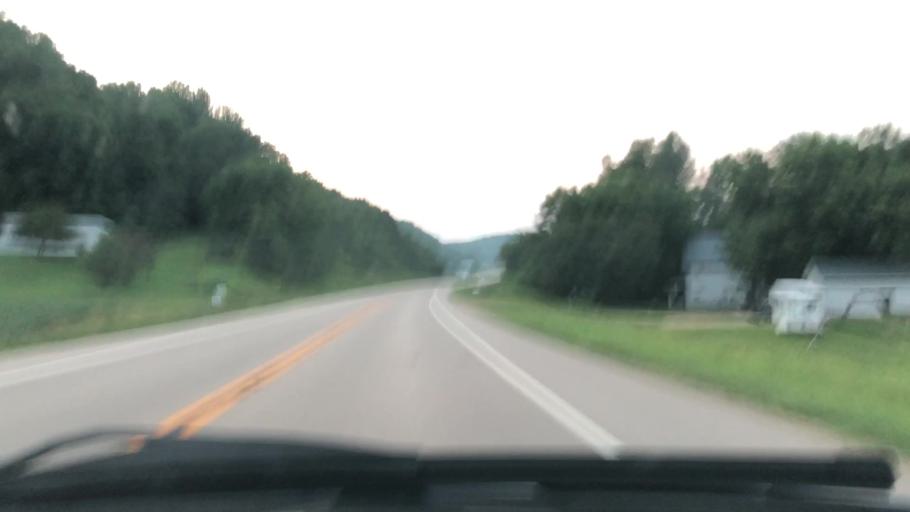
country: US
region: Wisconsin
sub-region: Richland County
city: Richland Center
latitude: 43.3585
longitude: -90.5571
